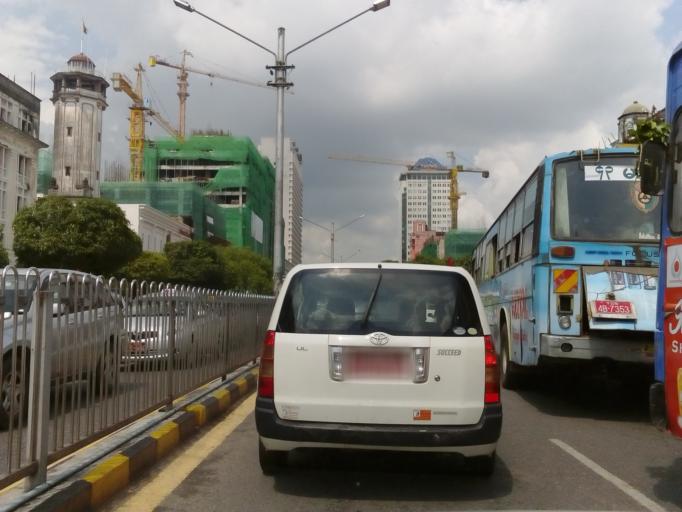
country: MM
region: Yangon
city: Yangon
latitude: 16.7753
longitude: 96.1589
